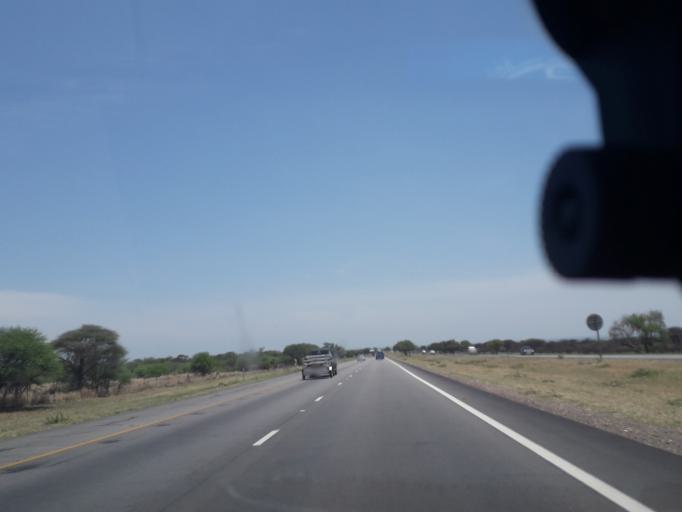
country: ZA
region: North-West
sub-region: Bojanala Platinum District Municipality
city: Makapanstad
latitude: -25.1550
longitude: 28.3082
